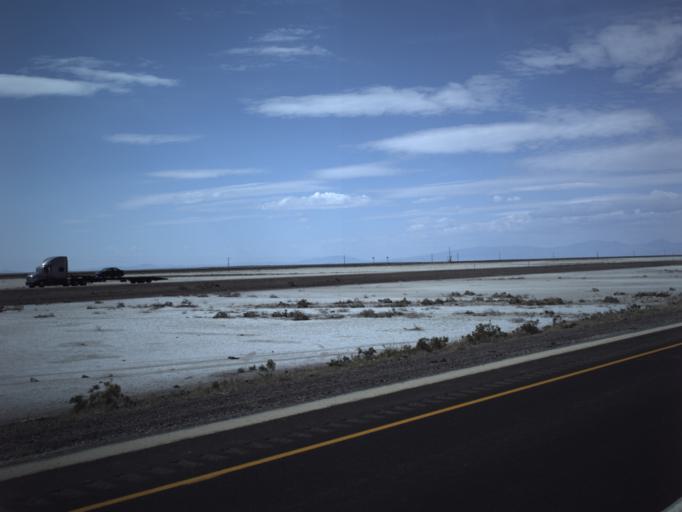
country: US
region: Utah
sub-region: Tooele County
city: Wendover
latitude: 40.7316
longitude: -113.4889
